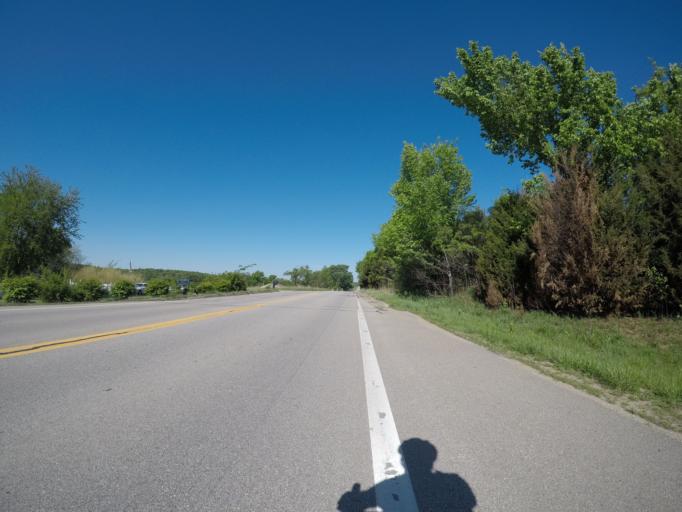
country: US
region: Kansas
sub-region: Douglas County
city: Lawrence
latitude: 38.9713
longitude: -95.4525
